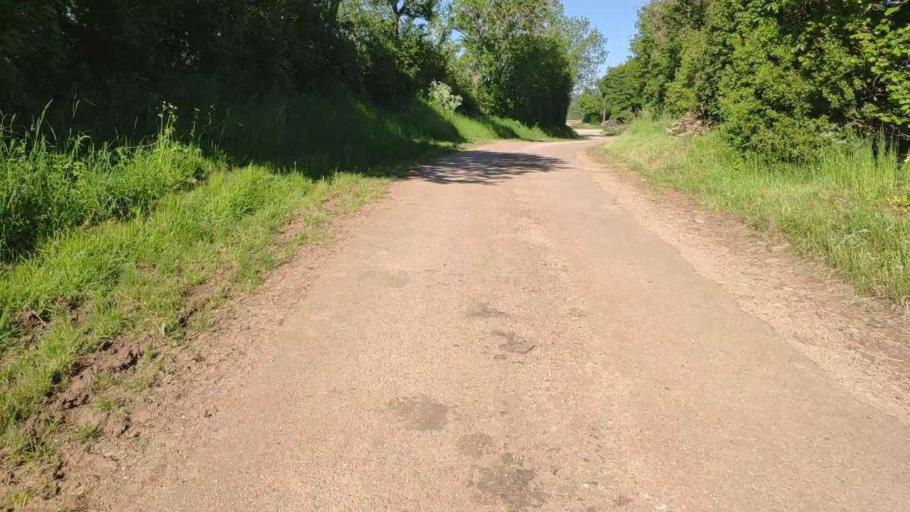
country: FR
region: Franche-Comte
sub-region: Departement du Jura
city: Perrigny
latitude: 46.6837
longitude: 5.6515
